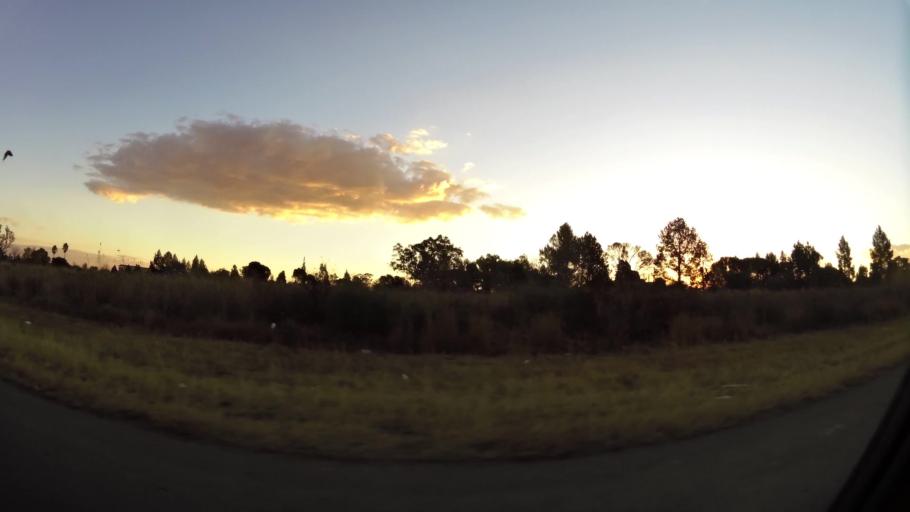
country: ZA
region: North-West
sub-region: Dr Kenneth Kaunda District Municipality
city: Potchefstroom
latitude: -26.6869
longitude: 27.0769
